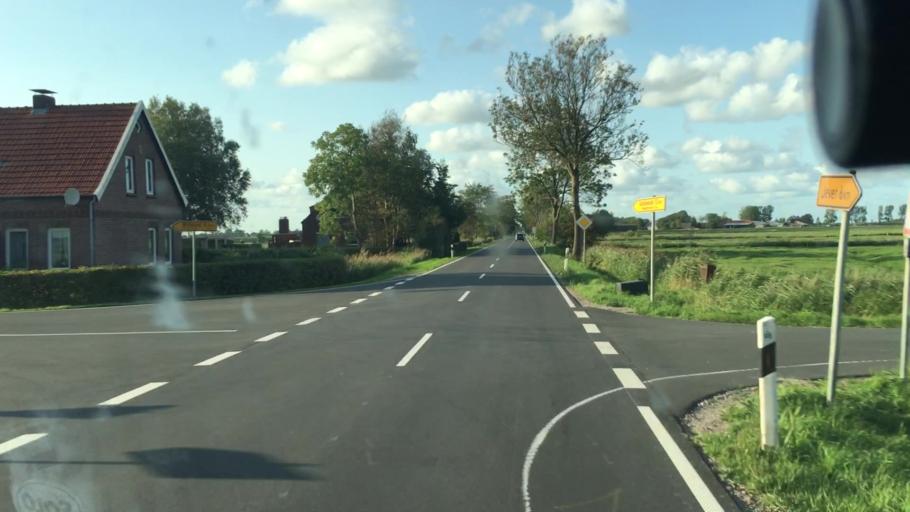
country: DE
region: Lower Saxony
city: Jever
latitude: 53.6157
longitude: 7.8665
